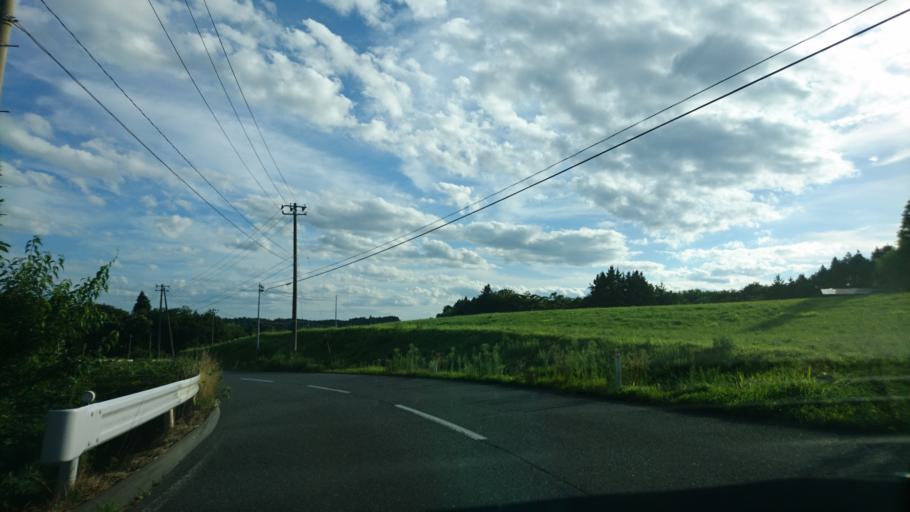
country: JP
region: Iwate
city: Ichinoseki
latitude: 38.8773
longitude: 141.1991
